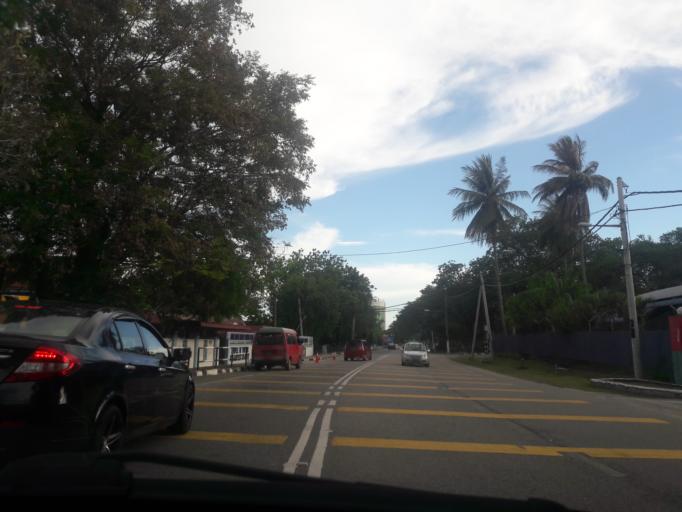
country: MY
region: Kedah
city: Sungai Petani
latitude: 5.6511
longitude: 100.4894
